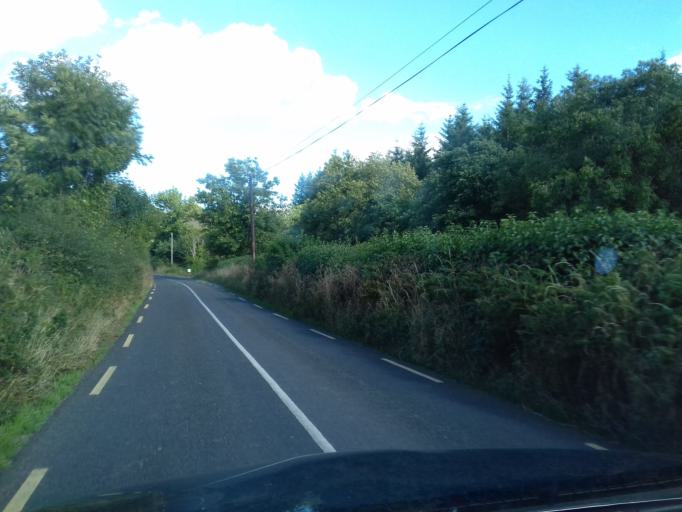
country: IE
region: Leinster
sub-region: Kilkenny
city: Thomastown
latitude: 52.5365
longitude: -7.0985
